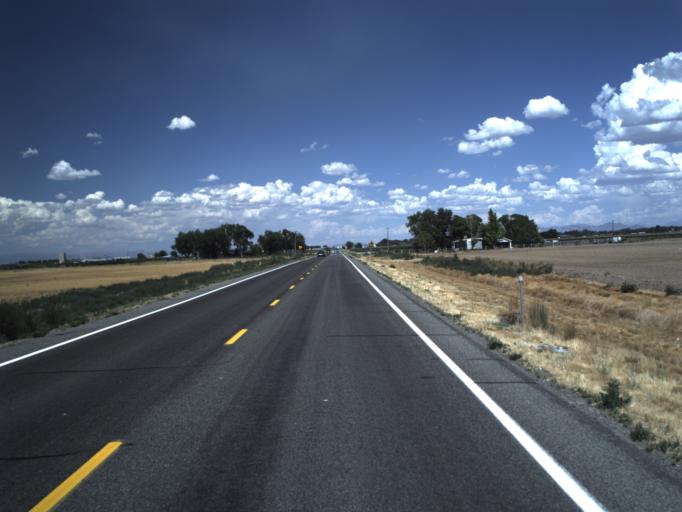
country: US
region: Utah
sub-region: Millard County
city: Delta
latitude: 39.3350
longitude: -112.6087
